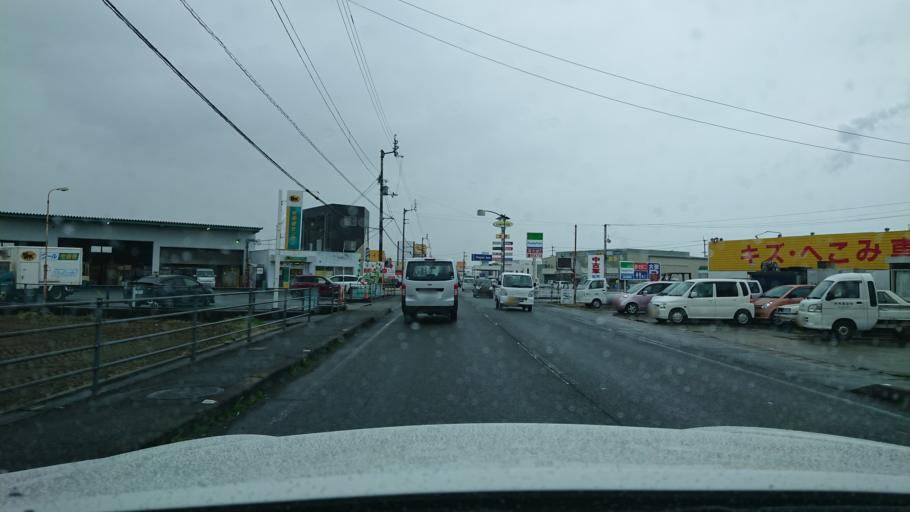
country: JP
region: Tokushima
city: Ishii
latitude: 34.0848
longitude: 134.4955
